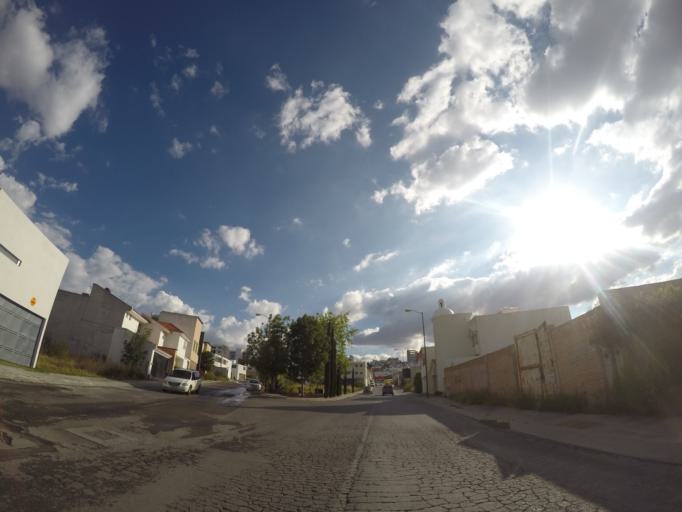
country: MX
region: San Luis Potosi
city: Escalerillas
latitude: 22.1250
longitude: -101.0278
